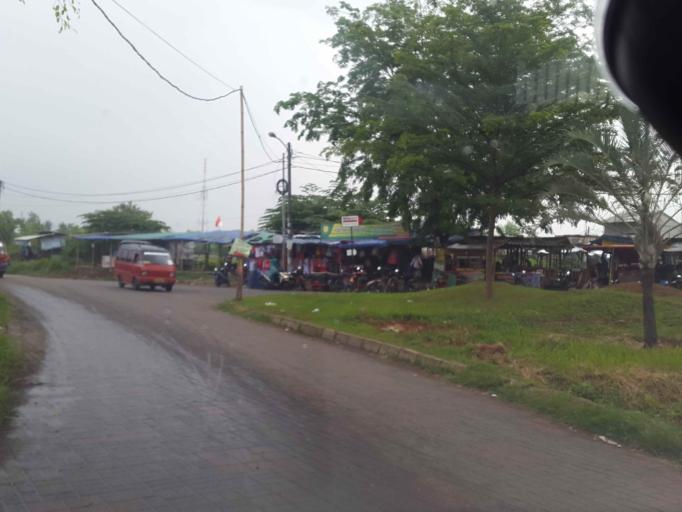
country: ID
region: West Java
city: Cikarang
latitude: -6.2774
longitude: 107.1788
